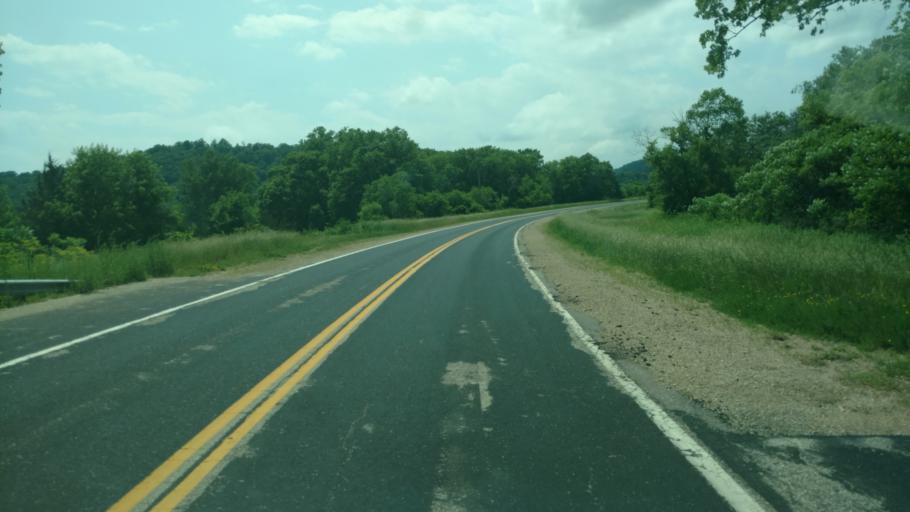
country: US
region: Wisconsin
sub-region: Monroe County
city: Cashton
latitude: 43.5569
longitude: -90.6483
